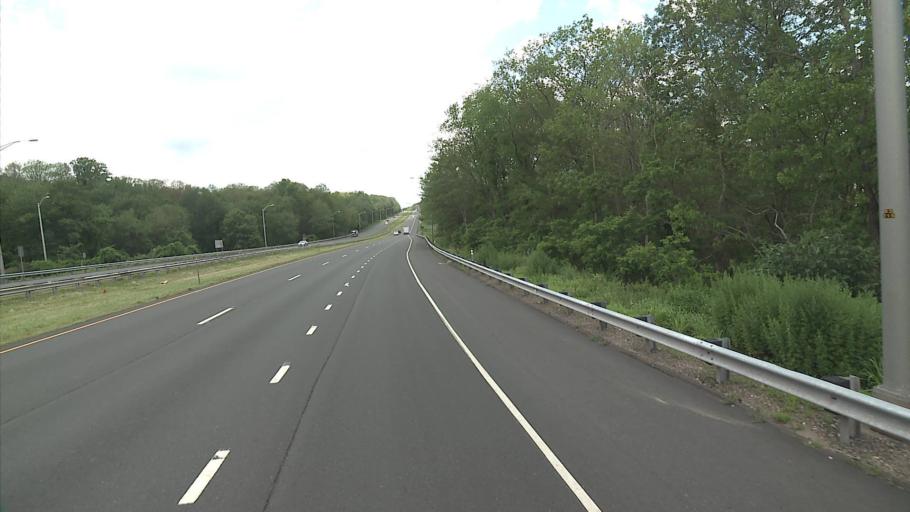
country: US
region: Connecticut
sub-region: Middlesex County
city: Higganum
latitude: 41.5143
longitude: -72.6000
